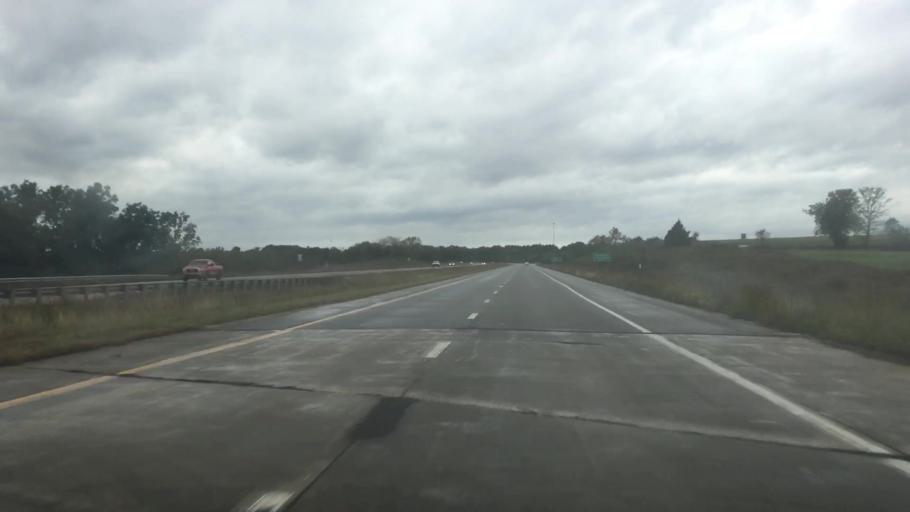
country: US
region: Kansas
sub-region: Miami County
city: Osawatomie
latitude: 38.5164
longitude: -94.9185
